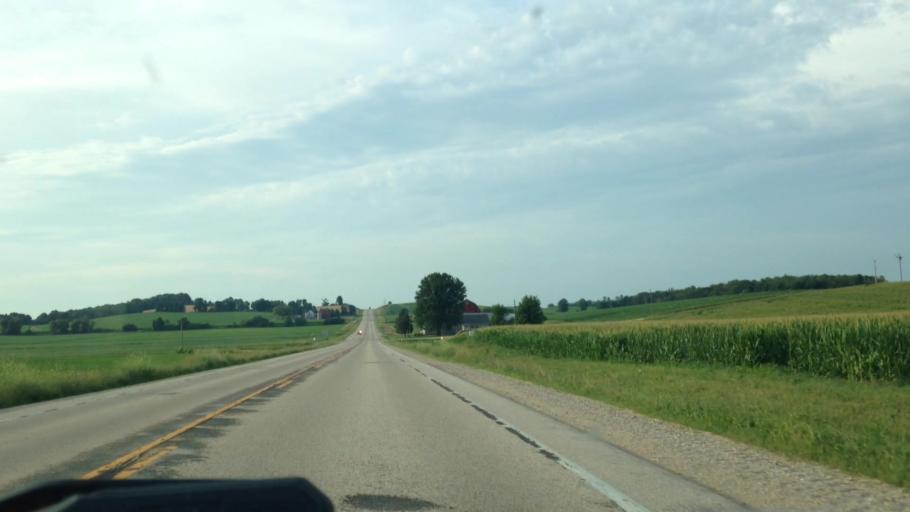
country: US
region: Wisconsin
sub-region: Dodge County
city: Theresa
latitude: 43.4690
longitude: -88.4501
